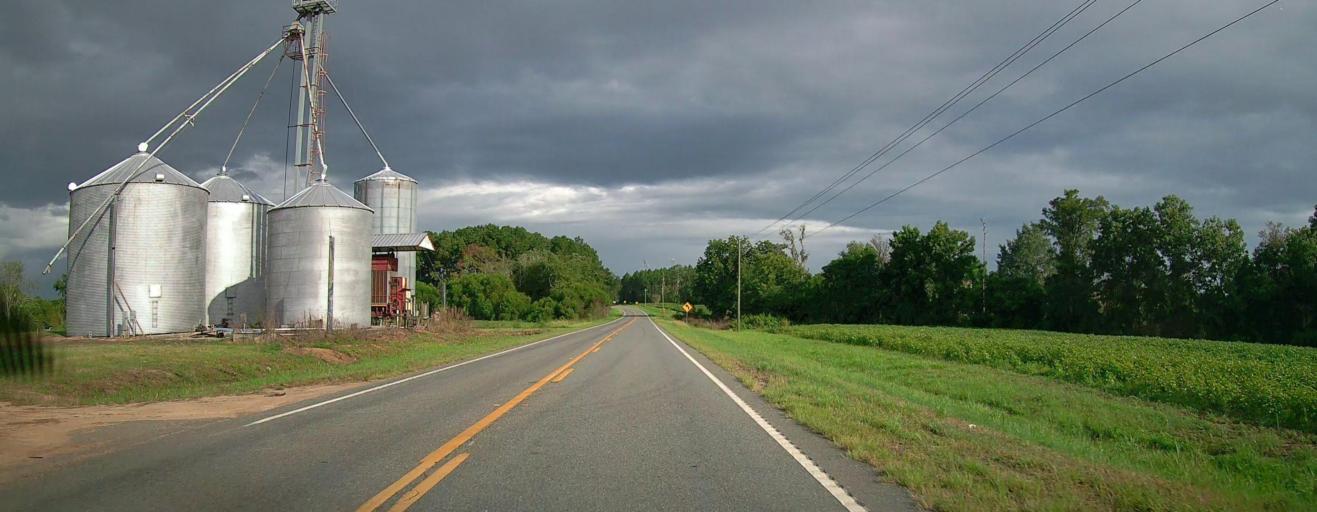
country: US
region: Georgia
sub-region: Coffee County
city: Nicholls
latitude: 31.3472
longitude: -82.6116
